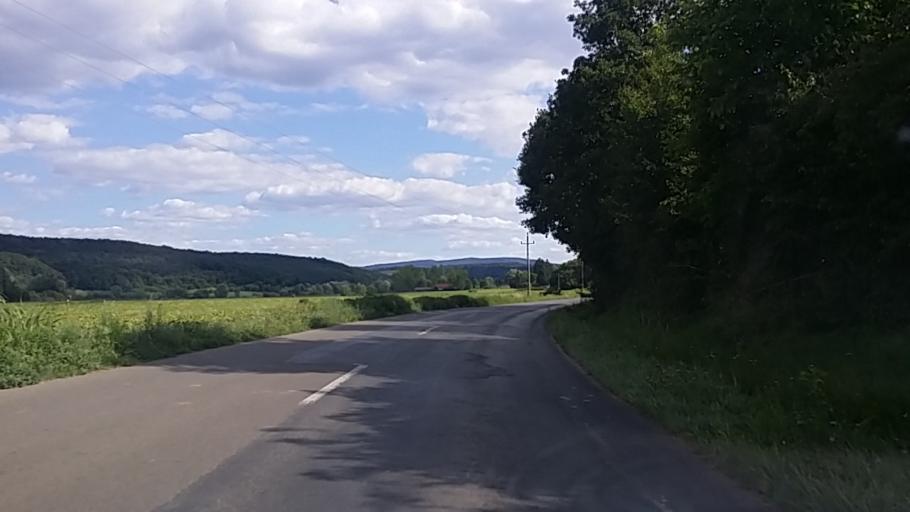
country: HU
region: Baranya
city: Sasd
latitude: 46.1831
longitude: 18.0835
